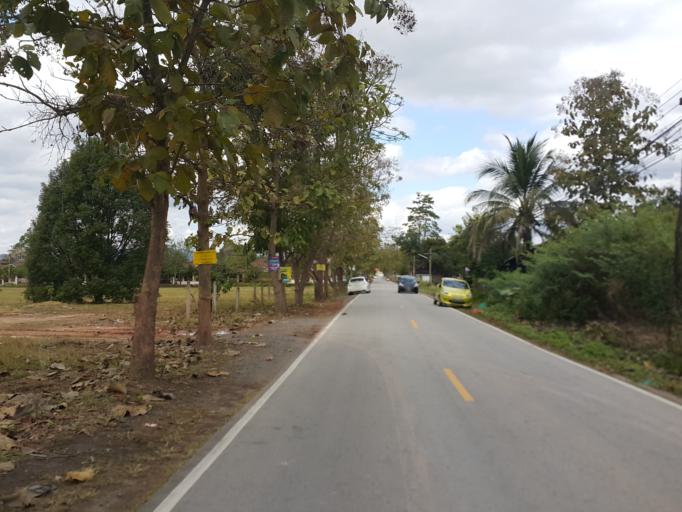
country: TH
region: Chiang Mai
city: San Sai
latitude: 18.8556
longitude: 99.1421
